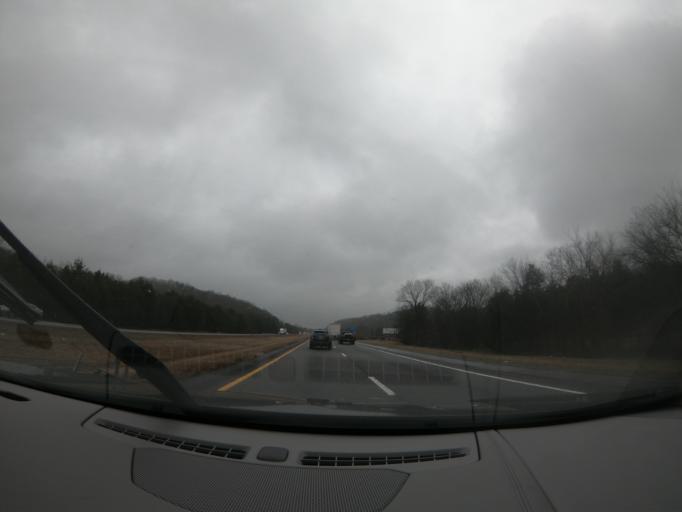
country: US
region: Tennessee
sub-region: Rutherford County
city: Plainview
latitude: 35.6441
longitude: -86.2526
